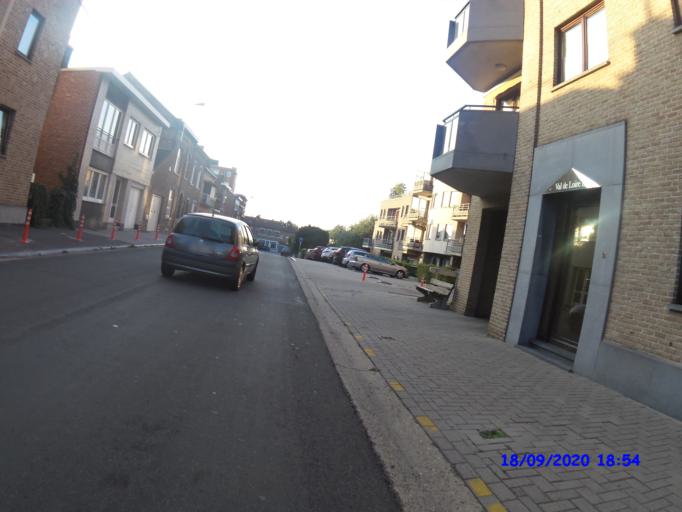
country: BE
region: Wallonia
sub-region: Province de Liege
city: Waremme
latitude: 50.6933
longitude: 5.2480
